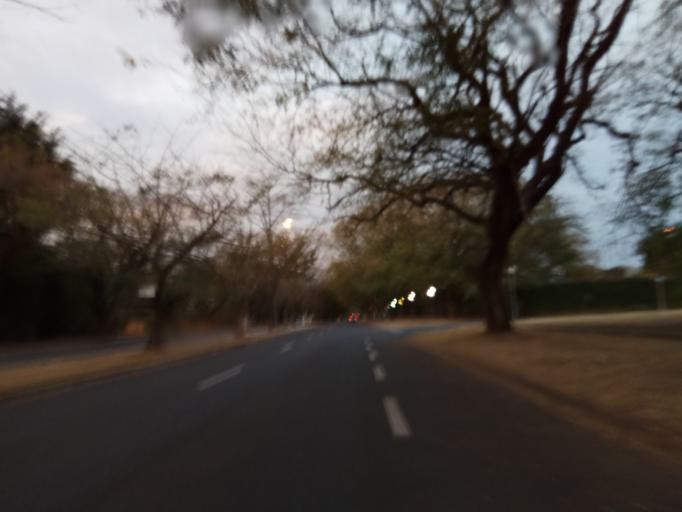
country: BR
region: Sao Paulo
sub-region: Piracicaba
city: Piracicaba
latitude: -22.7529
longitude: -47.5887
